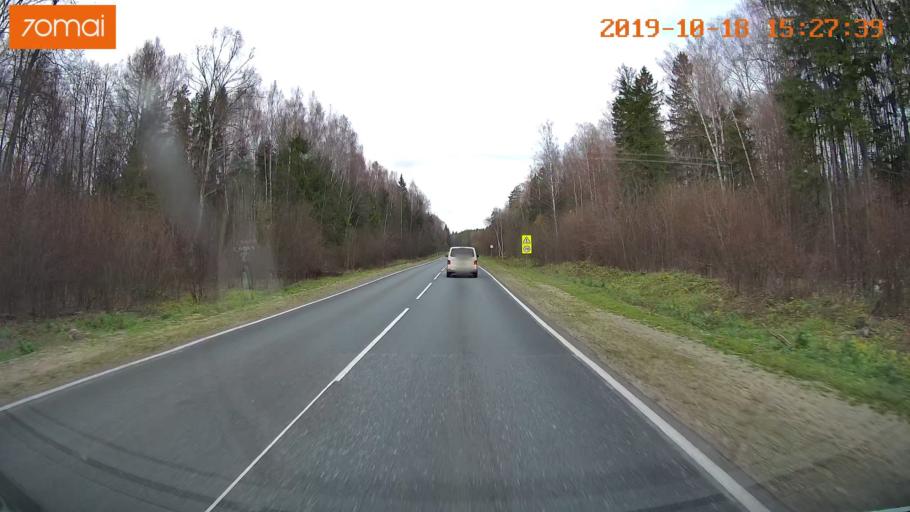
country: RU
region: Vladimir
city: Anopino
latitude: 55.7560
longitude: 40.6717
